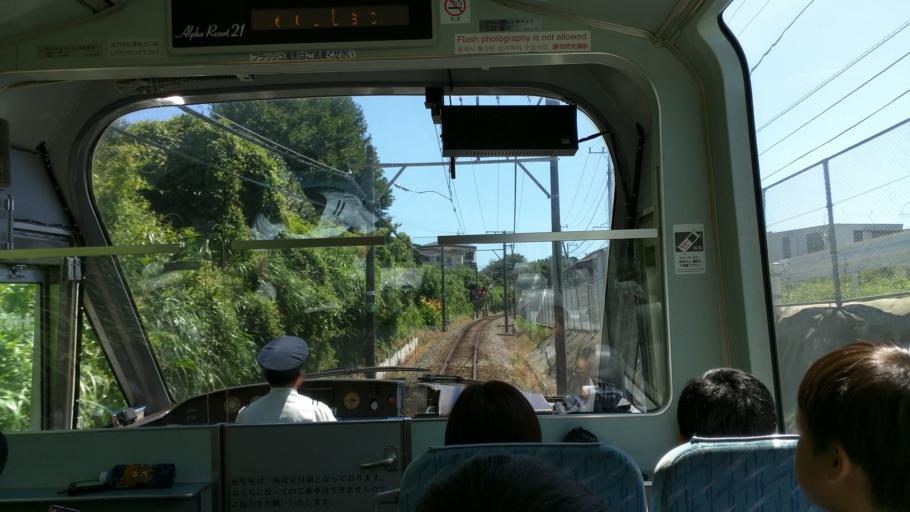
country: JP
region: Shizuoka
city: Ito
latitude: 34.9510
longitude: 139.1207
